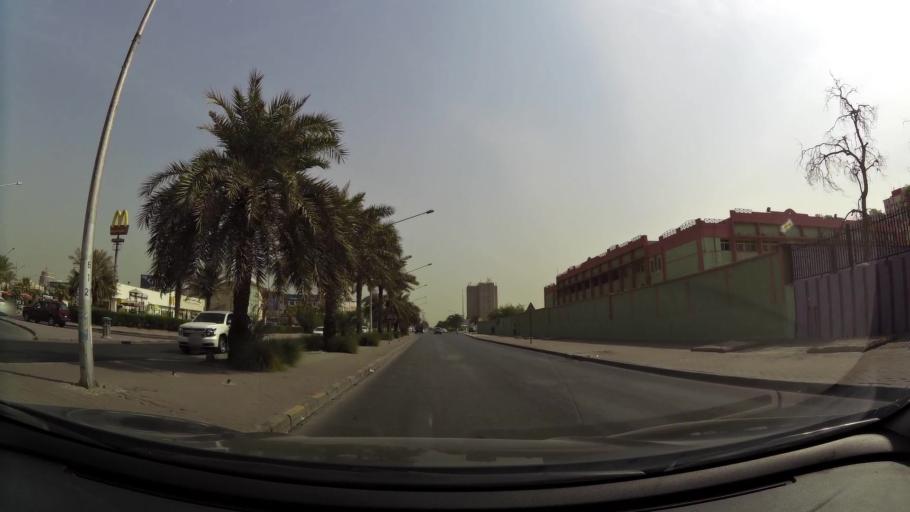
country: KW
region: Al Farwaniyah
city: Al Farwaniyah
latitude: 29.2594
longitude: 47.9379
